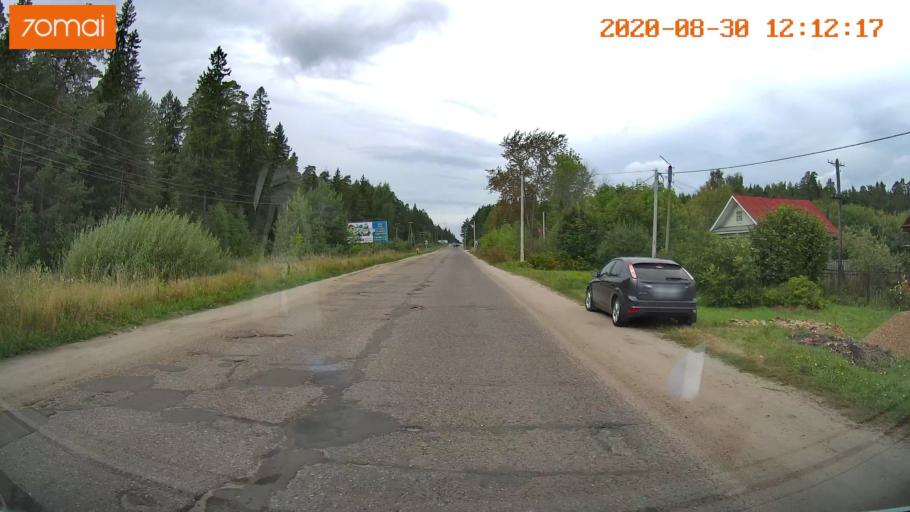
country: RU
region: Ivanovo
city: Yur'yevets
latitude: 57.3109
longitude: 43.0950
